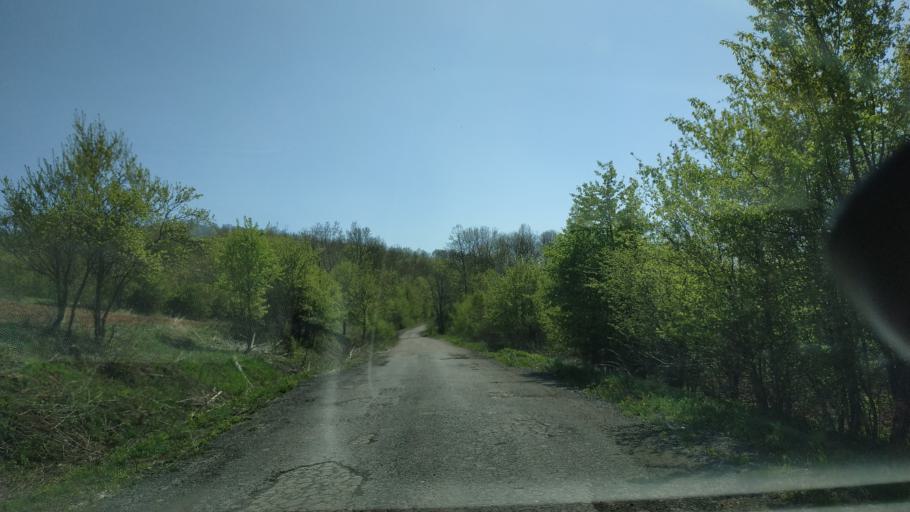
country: RS
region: Central Serbia
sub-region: Zajecarski Okrug
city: Soko Banja
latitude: 43.5090
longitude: 21.9004
